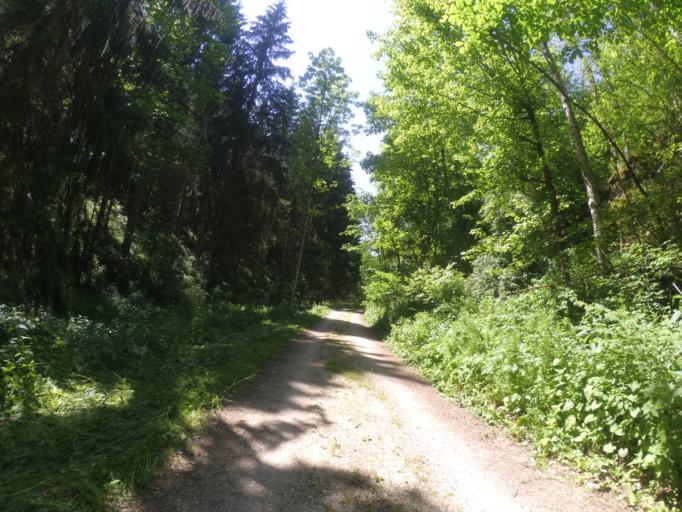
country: DE
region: Baden-Wuerttemberg
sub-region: Tuebingen Region
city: Berghulen
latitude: 48.4851
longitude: 9.7973
